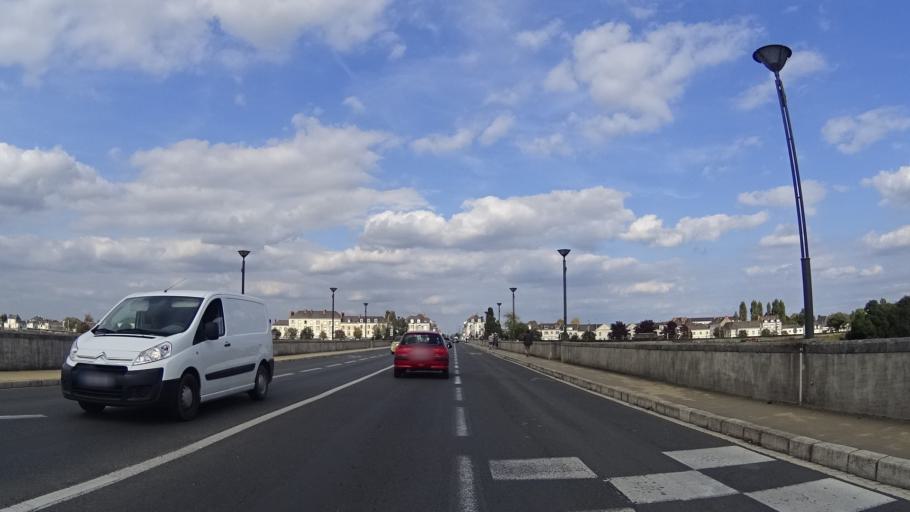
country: FR
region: Pays de la Loire
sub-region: Departement de Maine-et-Loire
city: Saumur
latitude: 47.2656
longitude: -0.0717
